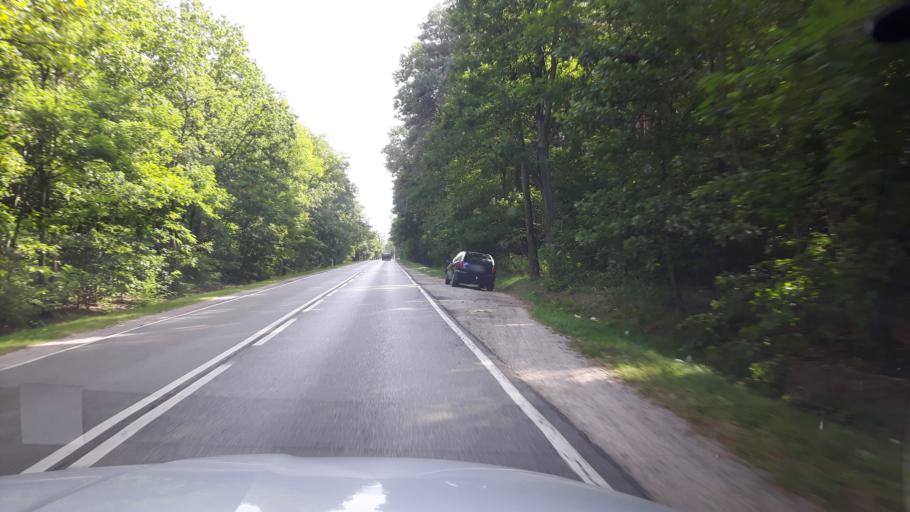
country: PL
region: Masovian Voivodeship
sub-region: Powiat wolominski
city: Radzymin
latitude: 52.3860
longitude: 21.2103
